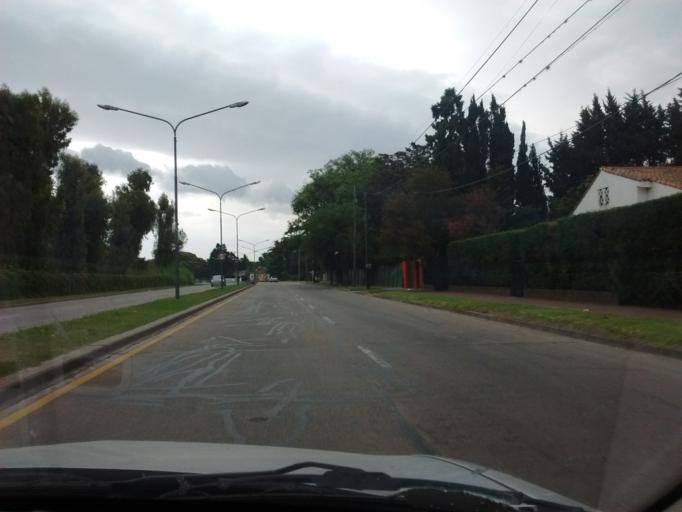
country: AR
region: Santa Fe
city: Funes
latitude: -32.9275
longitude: -60.7417
